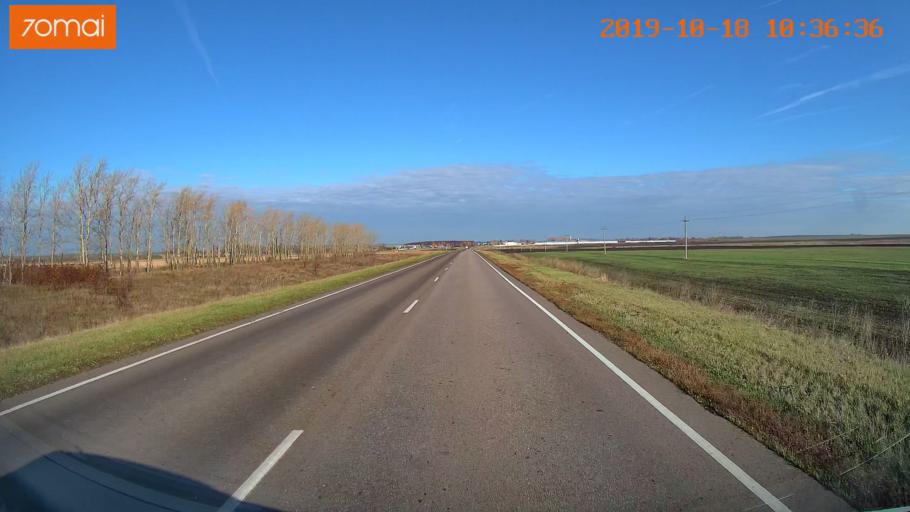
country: RU
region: Tula
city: Kurkino
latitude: 53.5509
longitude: 38.6268
